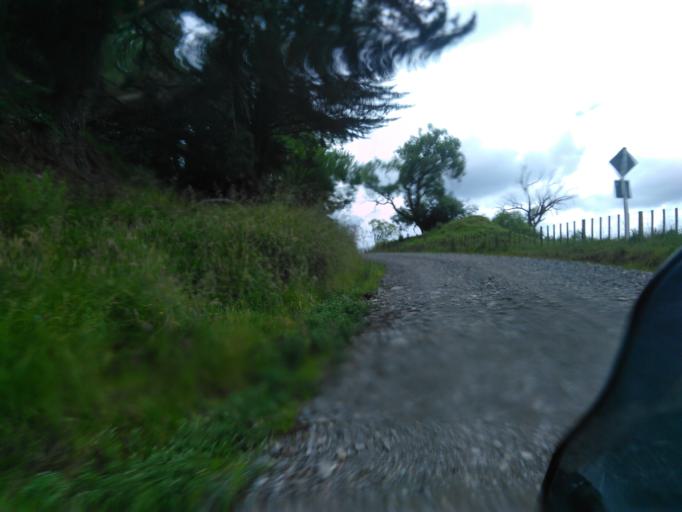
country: NZ
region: Gisborne
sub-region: Gisborne District
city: Gisborne
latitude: -38.0777
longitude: 178.0524
